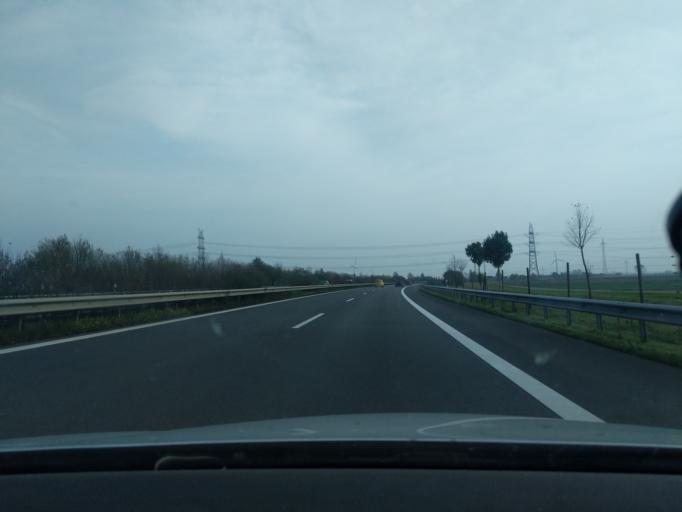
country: DE
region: Lower Saxony
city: Agathenburg
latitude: 53.5696
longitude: 9.5512
